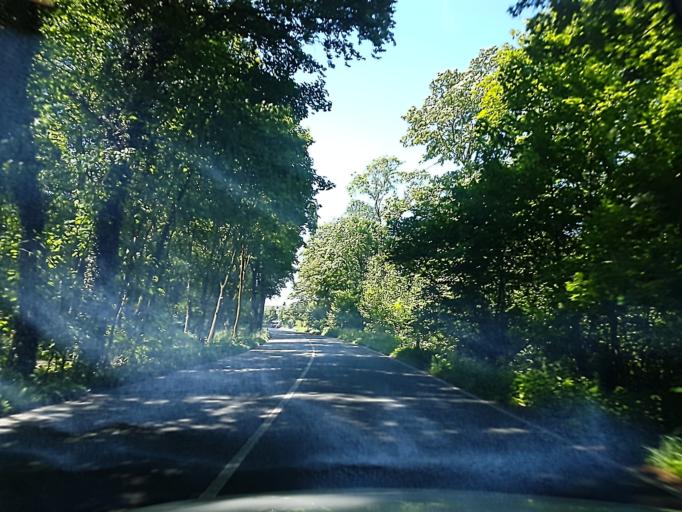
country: DE
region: North Rhine-Westphalia
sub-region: Regierungsbezirk Dusseldorf
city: Ratingen
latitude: 51.3343
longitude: 6.7967
